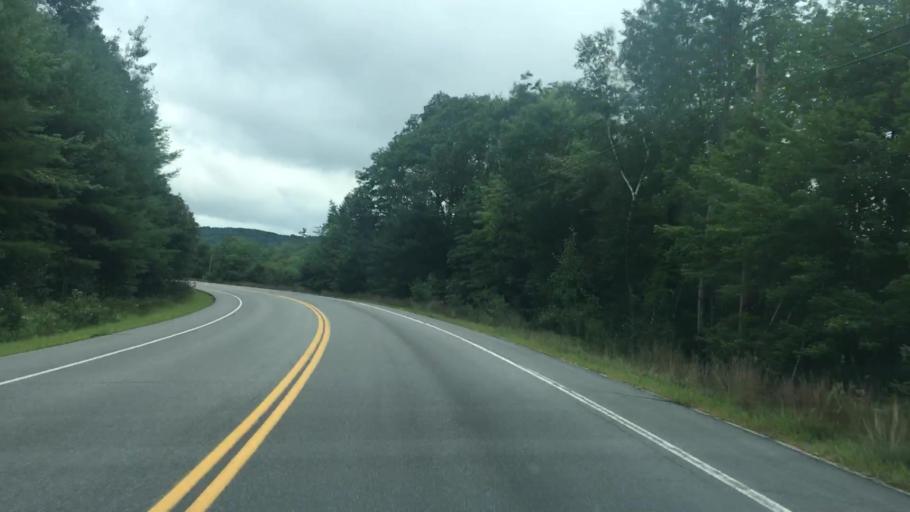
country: US
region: Maine
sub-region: York County
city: Cornish
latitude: 43.7793
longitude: -70.8249
